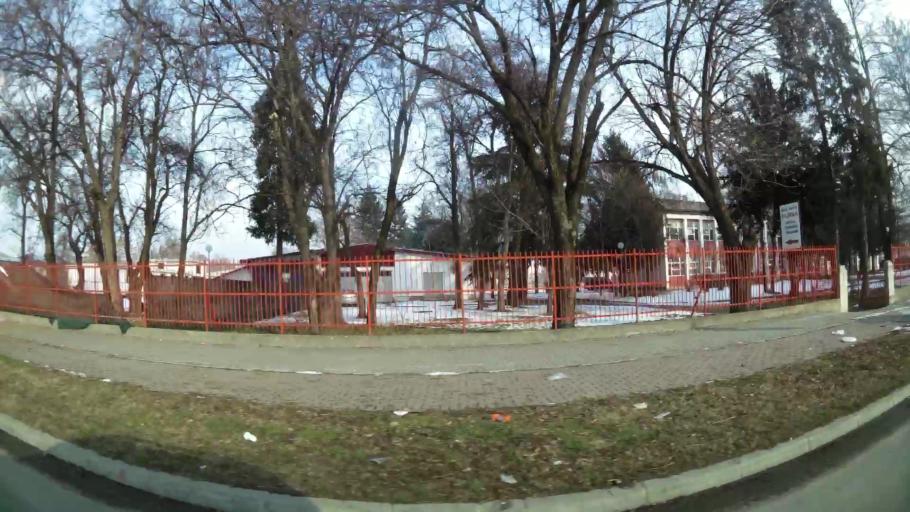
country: MK
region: Cair
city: Cair
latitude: 42.0222
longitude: 21.4349
